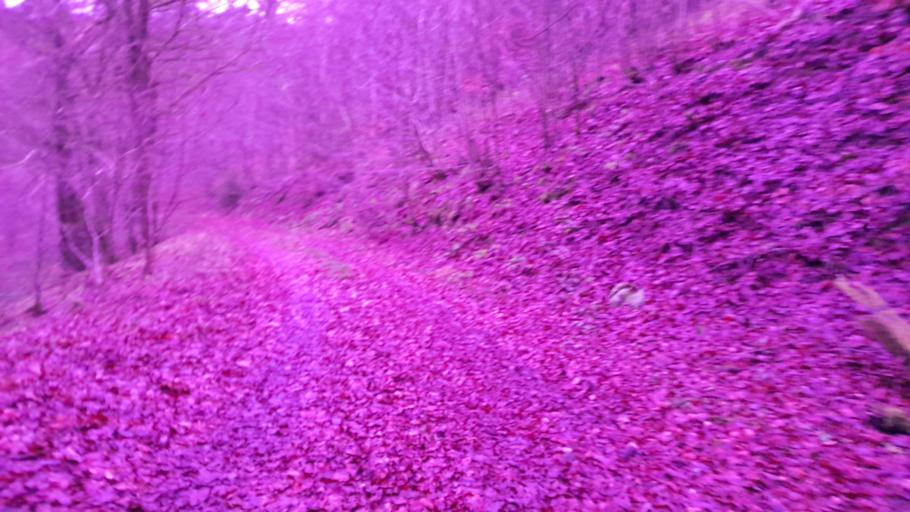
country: DE
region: Rheinland-Pfalz
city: Dasburg
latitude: 50.0759
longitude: 6.1038
